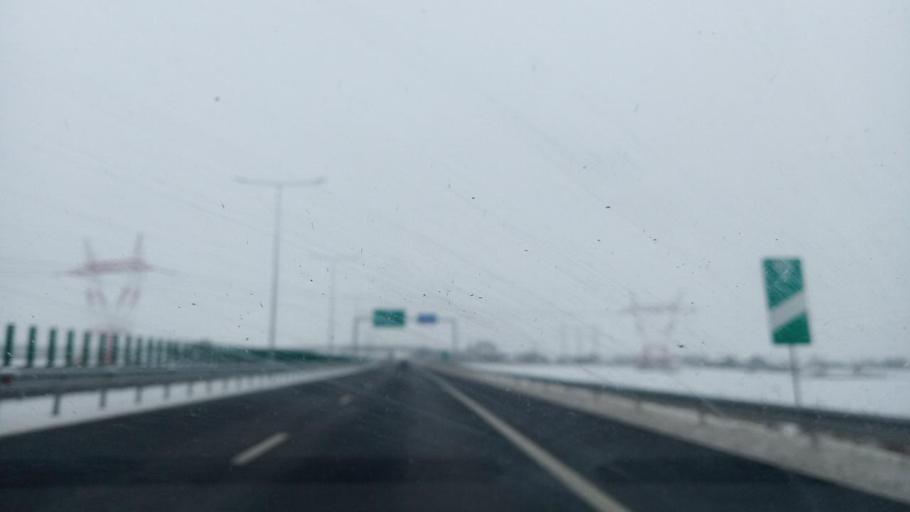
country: RO
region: Bacau
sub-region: Comuna Letea Veche
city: Holt
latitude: 46.5836
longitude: 26.9638
